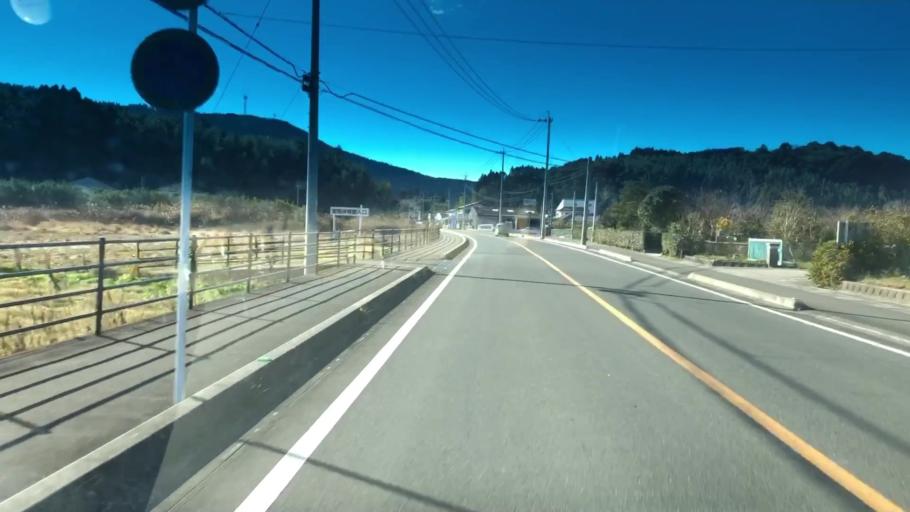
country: JP
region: Kagoshima
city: Satsumasendai
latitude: 31.8173
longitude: 130.2794
